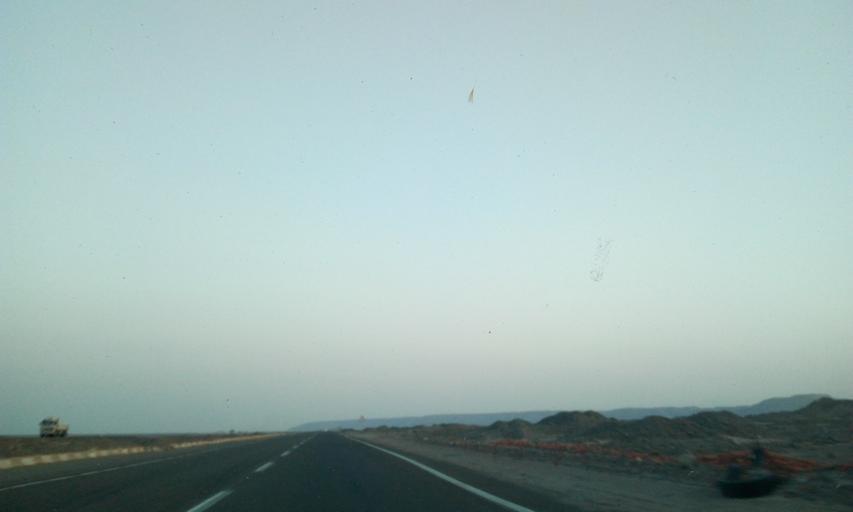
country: EG
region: Red Sea
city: El Gouna
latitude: 27.4757
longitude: 33.5832
